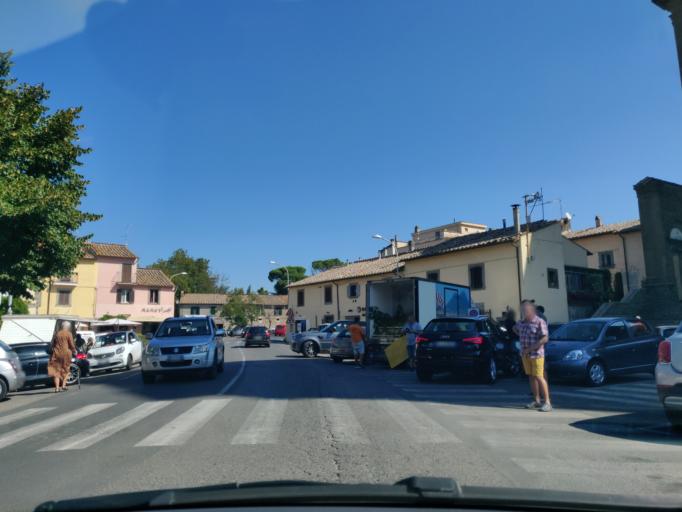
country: IT
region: Latium
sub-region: Provincia di Viterbo
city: Viterbo
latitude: 42.4296
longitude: 12.1288
